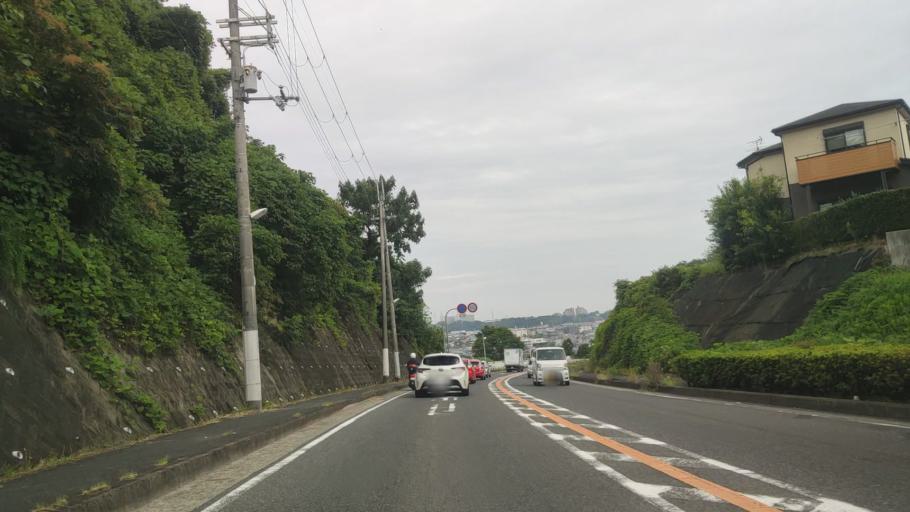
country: JP
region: Osaka
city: Tondabayashicho
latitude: 34.4361
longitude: 135.5579
